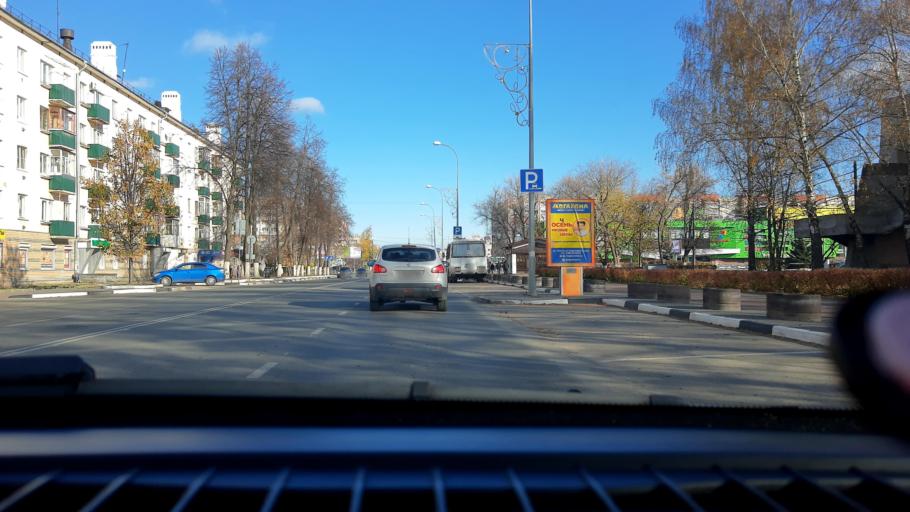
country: RU
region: Nizjnij Novgorod
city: Kstovo
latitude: 56.1507
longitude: 44.2048
